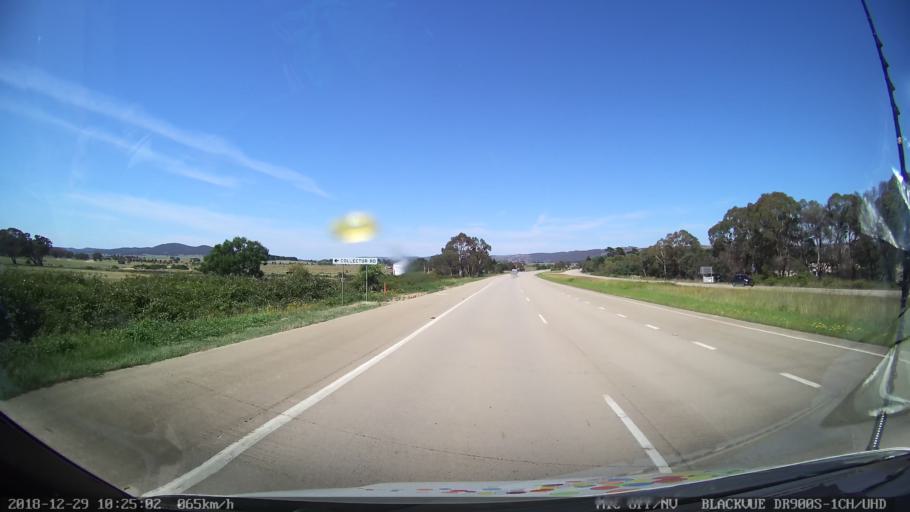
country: AU
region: New South Wales
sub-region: Yass Valley
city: Gundaroo
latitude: -34.9156
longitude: 149.4394
